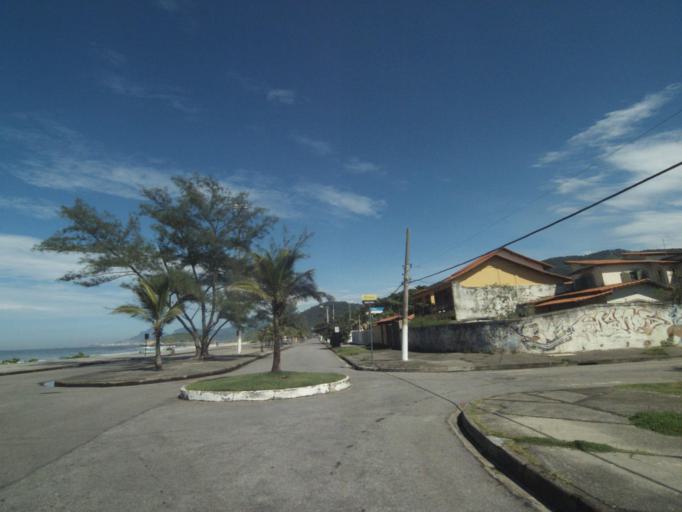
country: BR
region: Rio de Janeiro
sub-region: Niteroi
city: Niteroi
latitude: -22.9537
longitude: -43.0896
